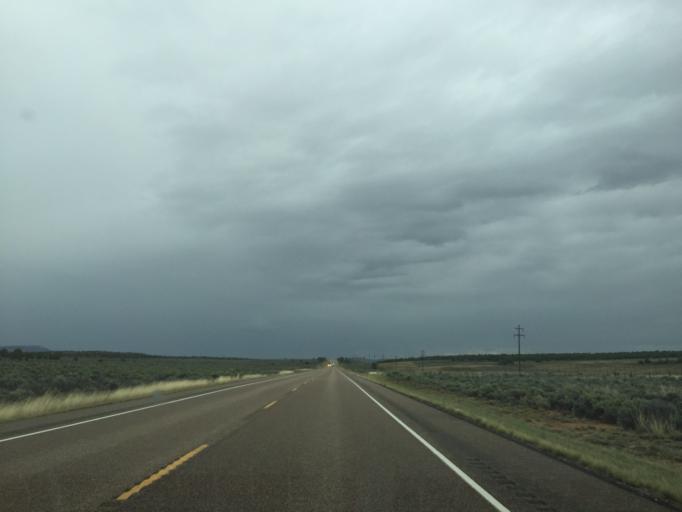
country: US
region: Utah
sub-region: Kane County
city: Kanab
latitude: 37.1366
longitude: -112.0825
